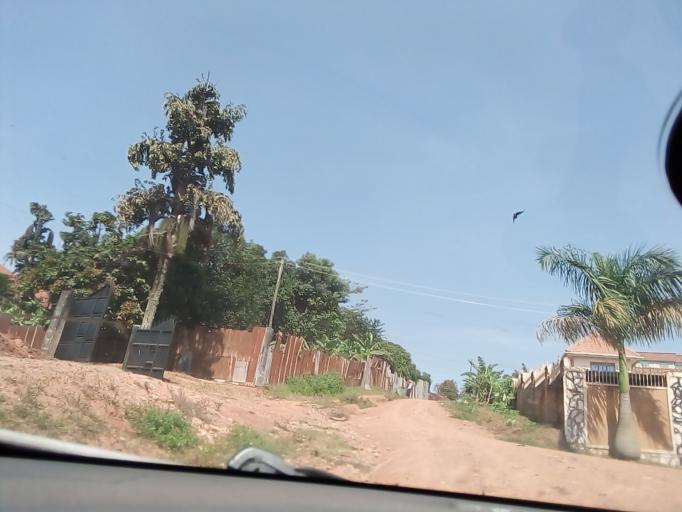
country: UG
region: Central Region
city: Masaka
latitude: -0.3528
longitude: 31.7428
